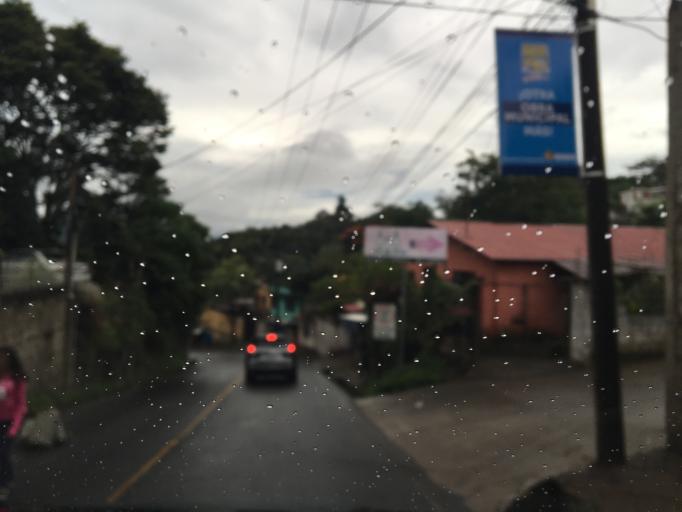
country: GT
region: Guatemala
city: Santa Catarina Pinula
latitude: 14.5503
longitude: -90.5098
